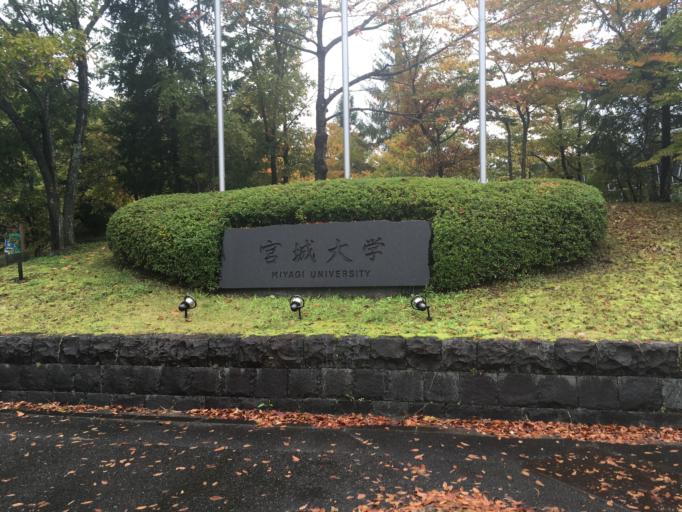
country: JP
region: Miyagi
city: Tomiya
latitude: 38.3485
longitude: 140.8419
